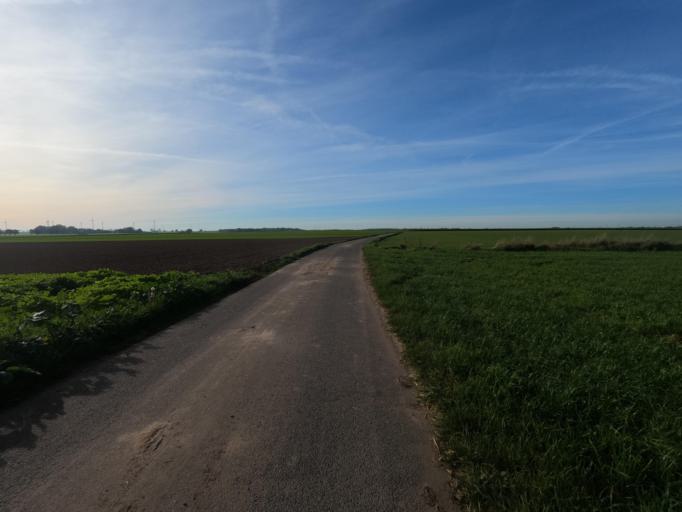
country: DE
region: North Rhine-Westphalia
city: Erkelenz
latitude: 51.0723
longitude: 6.3874
